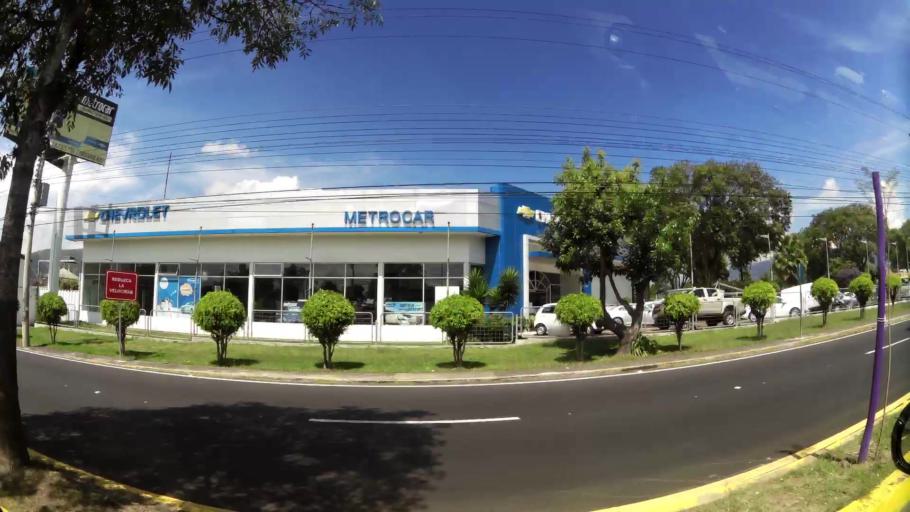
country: EC
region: Pichincha
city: Quito
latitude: -0.2114
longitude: -78.4136
